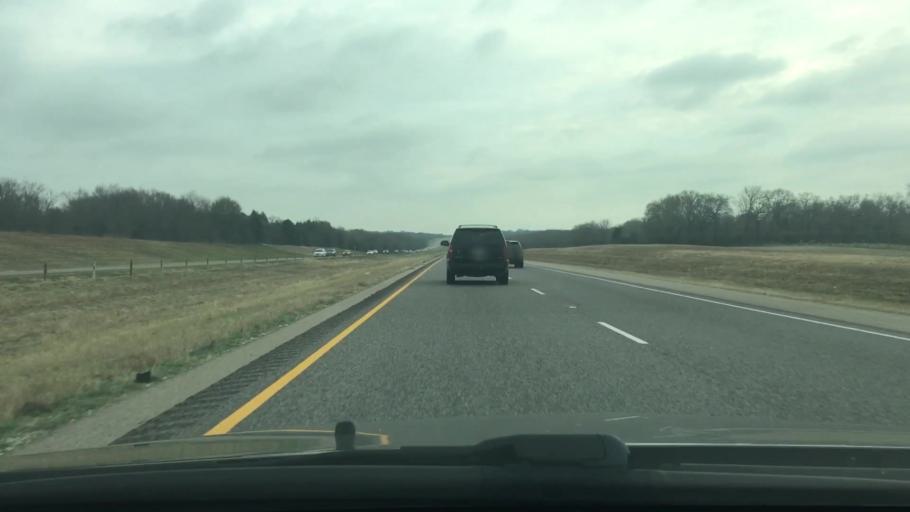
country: US
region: Texas
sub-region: Freestone County
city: Fairfield
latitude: 31.6612
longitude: -96.1619
